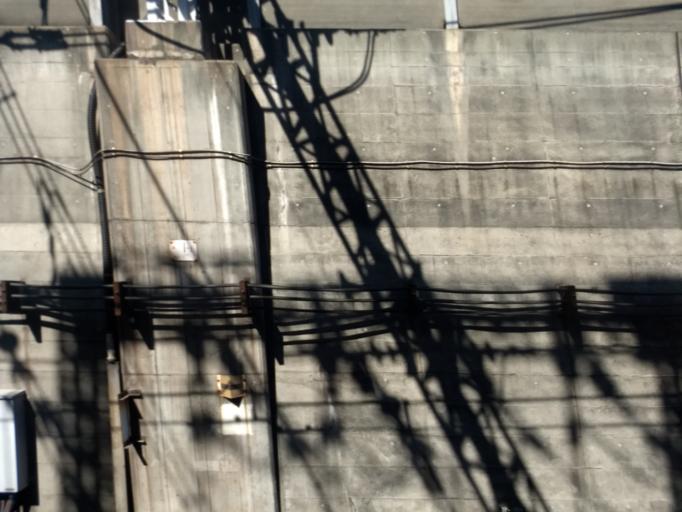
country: JP
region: Tokyo
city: Urayasu
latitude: 35.6614
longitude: 139.8110
